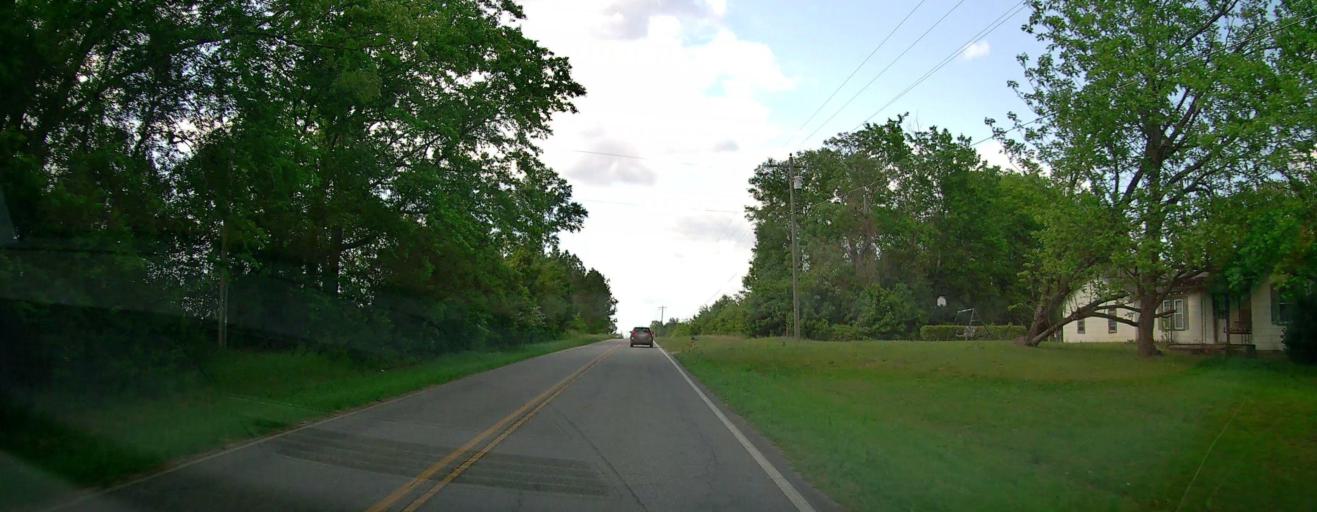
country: US
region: Georgia
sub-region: Laurens County
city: East Dublin
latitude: 32.5983
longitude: -82.8661
